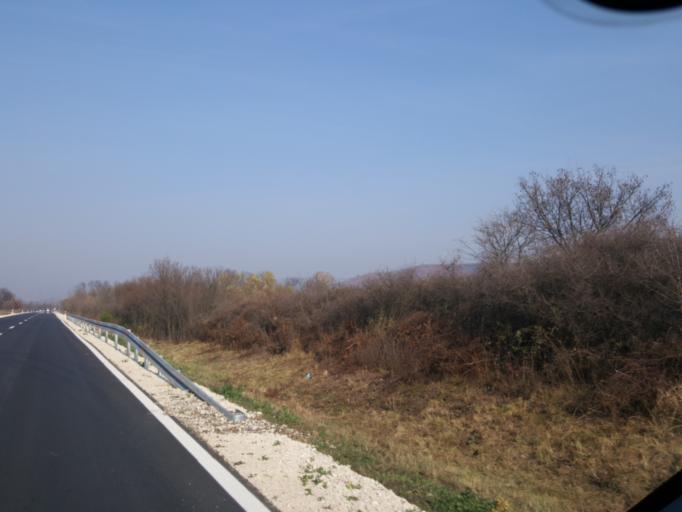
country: RS
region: Central Serbia
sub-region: Zajecarski Okrug
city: Zajecar
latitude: 43.9710
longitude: 22.2931
